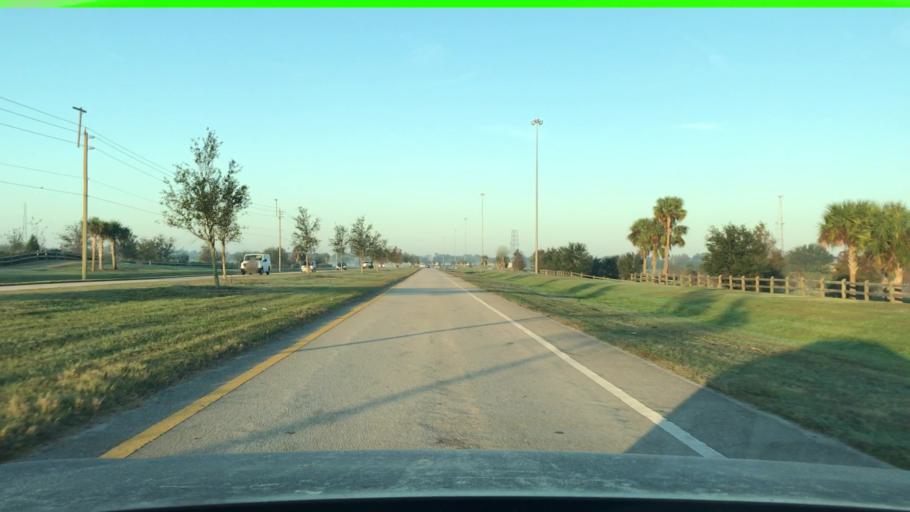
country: US
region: Florida
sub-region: Sarasota County
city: Fruitville
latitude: 27.3254
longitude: -82.4370
